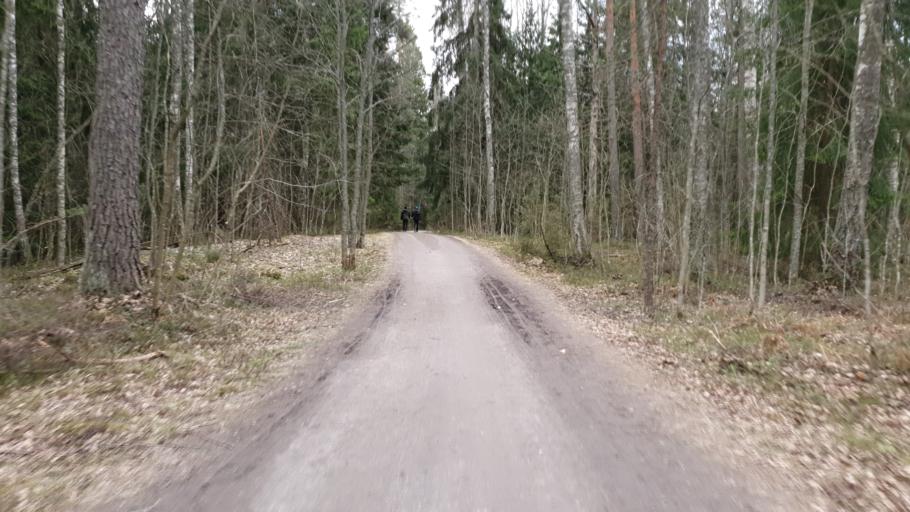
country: FI
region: Uusimaa
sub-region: Helsinki
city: Helsinki
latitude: 60.2702
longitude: 24.9255
